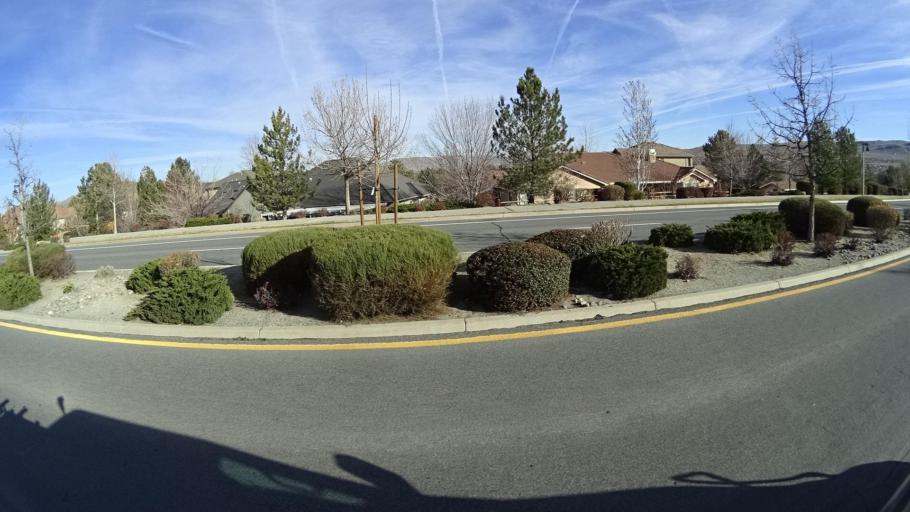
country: US
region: Nevada
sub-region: Washoe County
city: Spanish Springs
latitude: 39.6071
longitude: -119.6802
